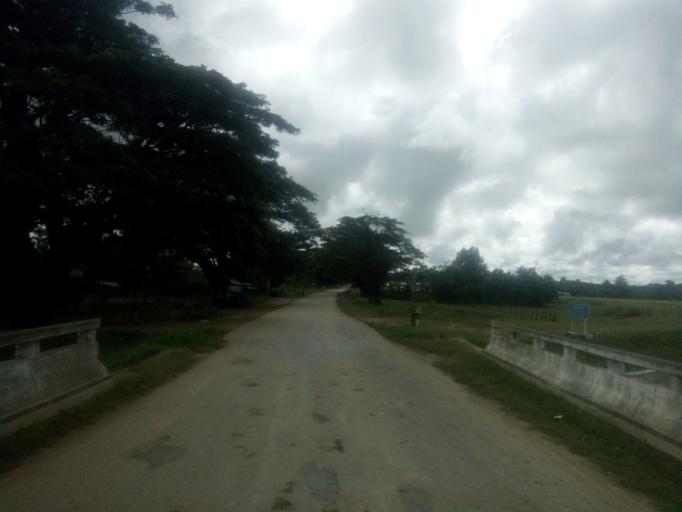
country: MM
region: Bago
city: Nyaunglebin
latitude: 17.9229
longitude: 96.5138
